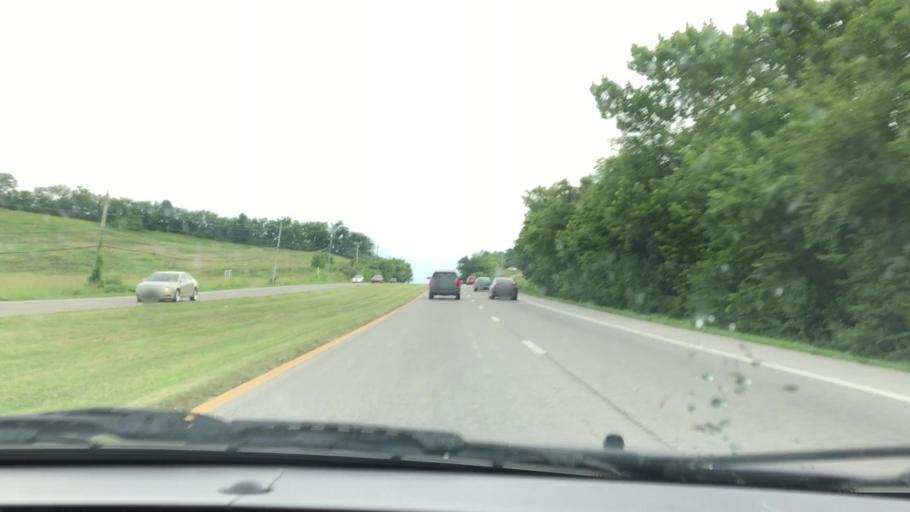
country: US
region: Tennessee
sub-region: Maury County
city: Columbia
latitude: 35.6548
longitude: -87.0096
